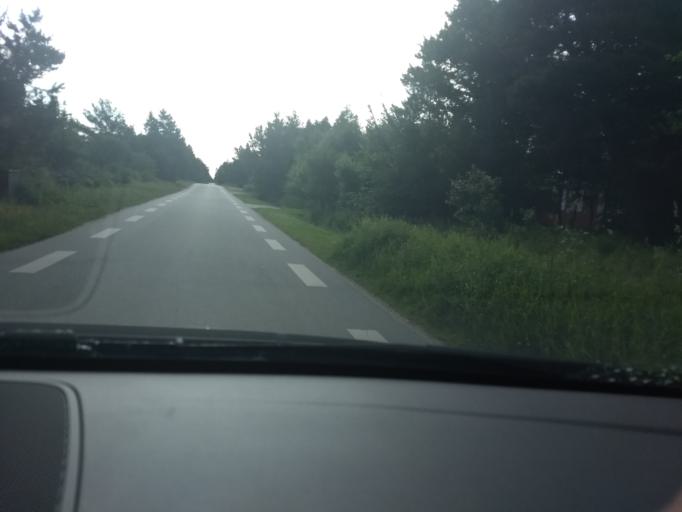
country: DE
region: Schleswig-Holstein
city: List
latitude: 55.1299
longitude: 8.5263
